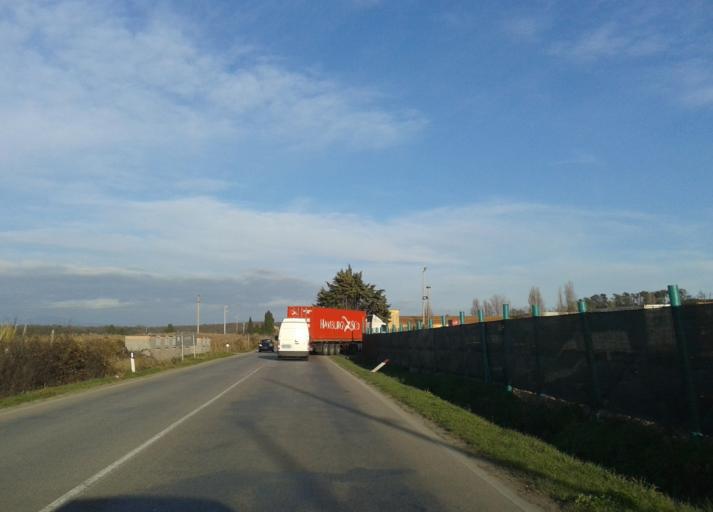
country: IT
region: Tuscany
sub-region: Provincia di Livorno
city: Livorno
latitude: 43.5704
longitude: 10.3661
